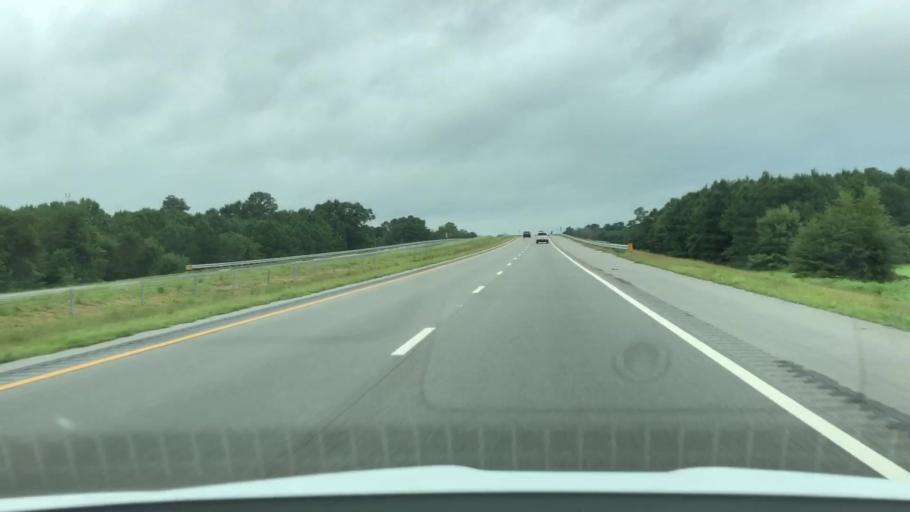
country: US
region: North Carolina
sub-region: Wayne County
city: Elroy
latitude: 35.3386
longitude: -77.8443
